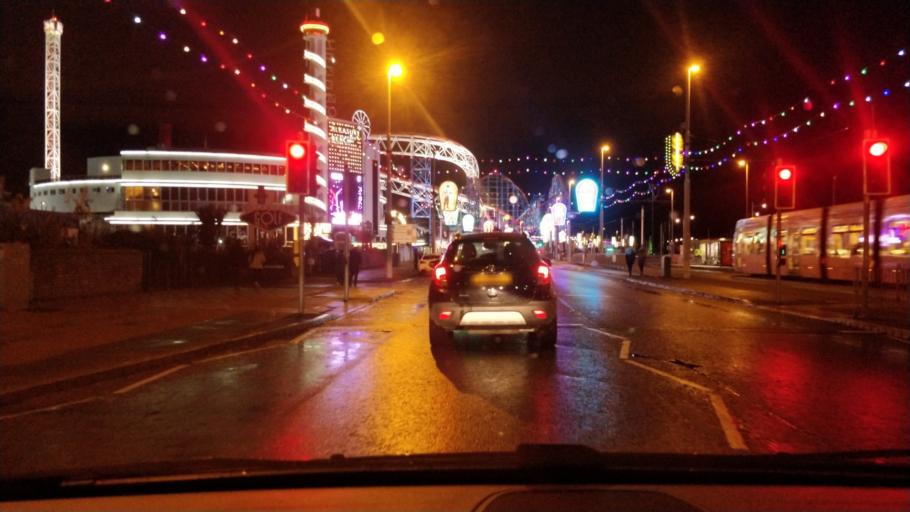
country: GB
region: England
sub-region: Blackpool
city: Blackpool
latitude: 53.7946
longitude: -3.0562
